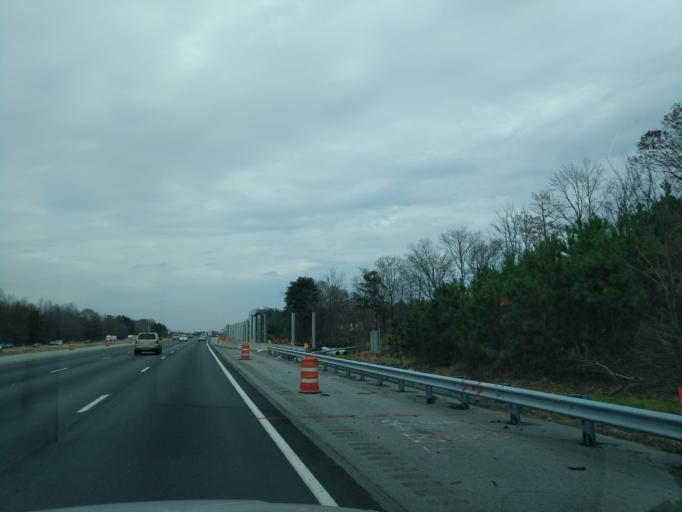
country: US
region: Georgia
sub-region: Gwinnett County
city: Sugar Hill
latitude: 34.0525
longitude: -84.0139
